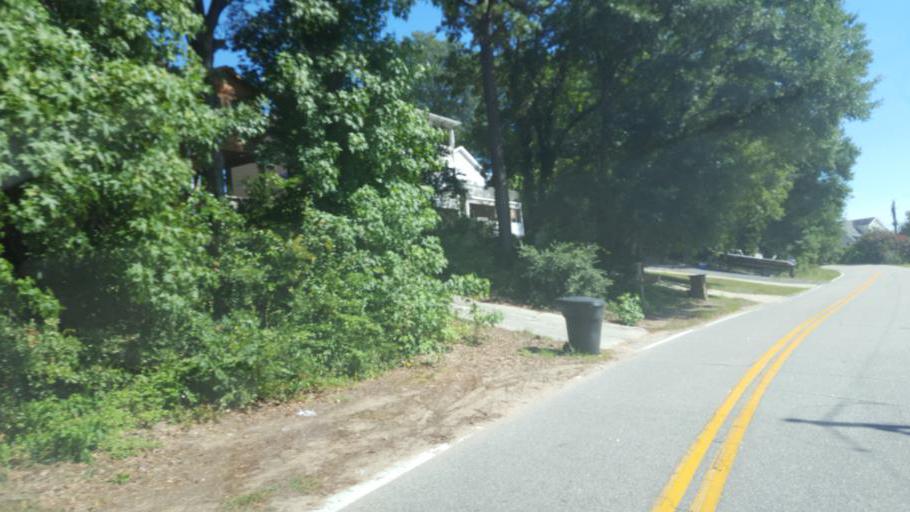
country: US
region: North Carolina
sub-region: Dare County
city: Kill Devil Hills
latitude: 36.0139
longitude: -75.7114
